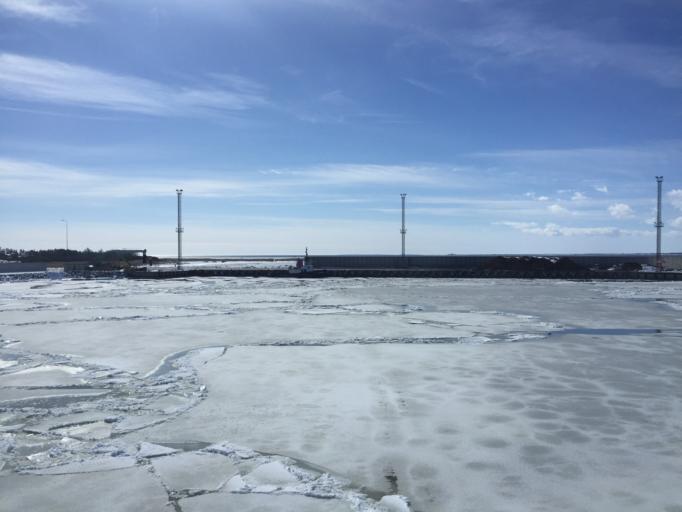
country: EE
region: Laeaene
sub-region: Lihula vald
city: Lihula
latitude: 58.5761
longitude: 23.5065
